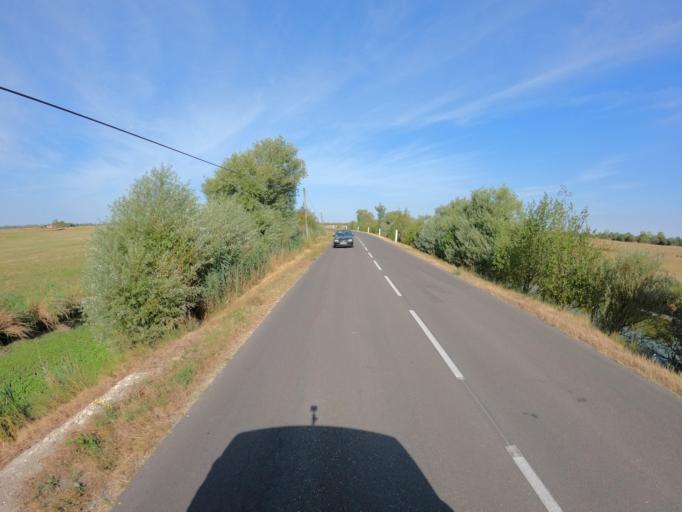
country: FR
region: Pays de la Loire
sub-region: Departement de la Vendee
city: Soullans
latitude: 46.8085
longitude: -1.9268
